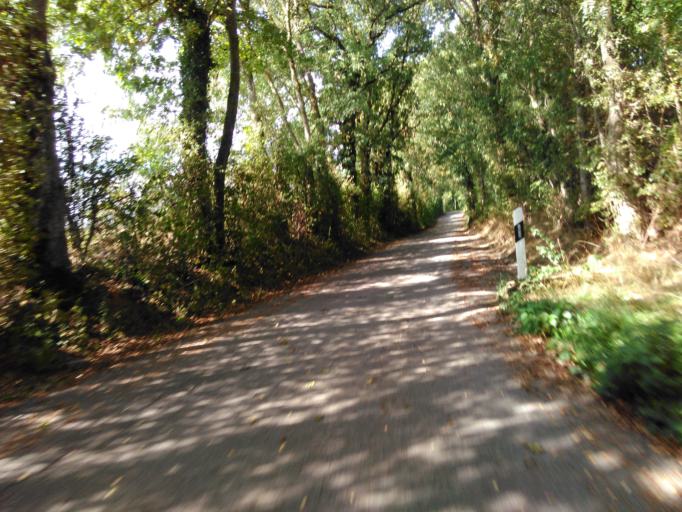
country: LU
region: Luxembourg
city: Soleuvre
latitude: 49.5288
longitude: 5.9319
